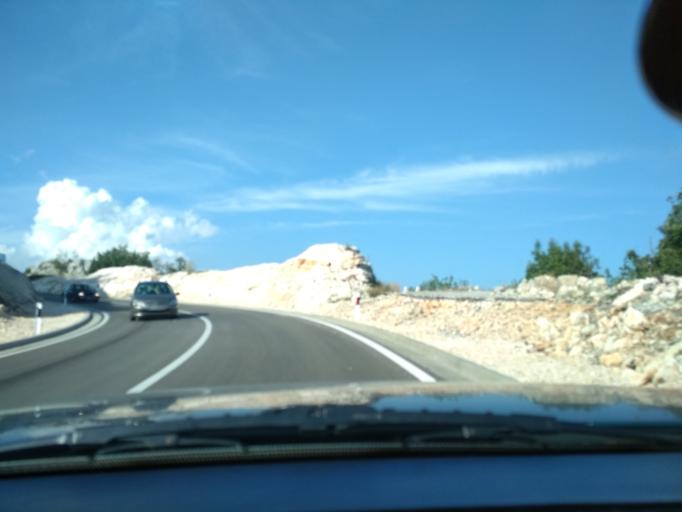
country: ME
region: Cetinje
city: Cetinje
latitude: 42.4061
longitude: 18.8883
